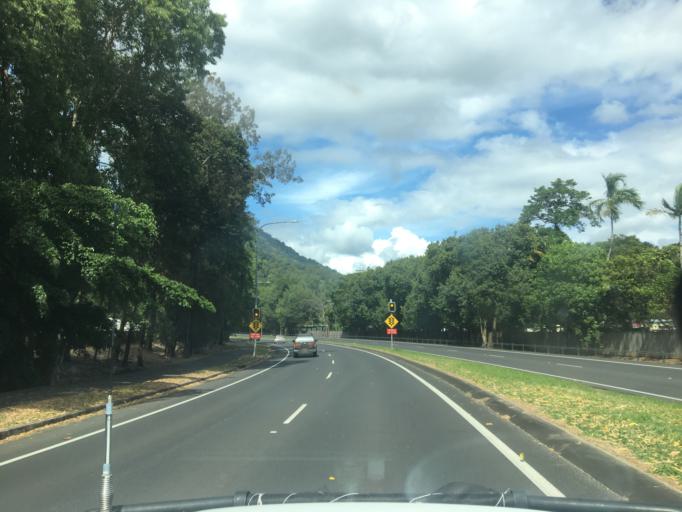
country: AU
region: Queensland
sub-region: Cairns
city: Redlynch
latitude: -16.9020
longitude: 145.7091
